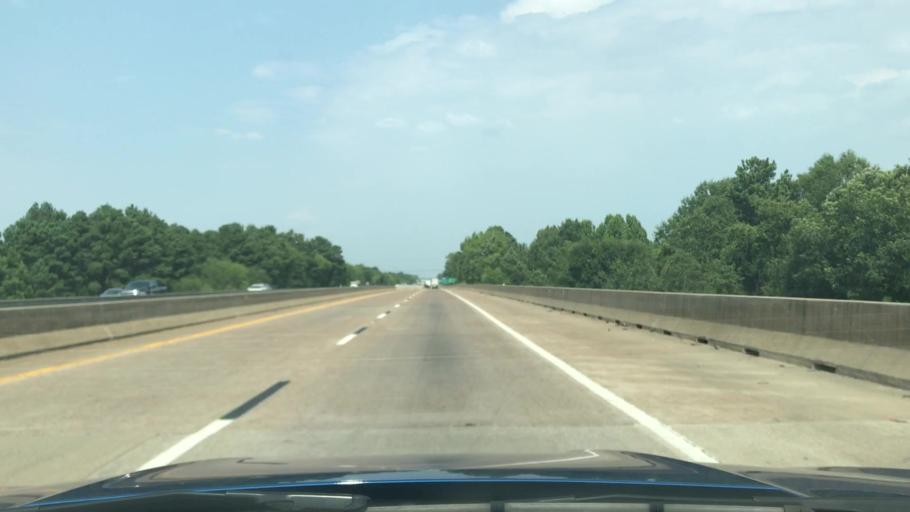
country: US
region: Texas
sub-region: Gregg County
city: Longview
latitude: 32.4374
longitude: -94.7444
